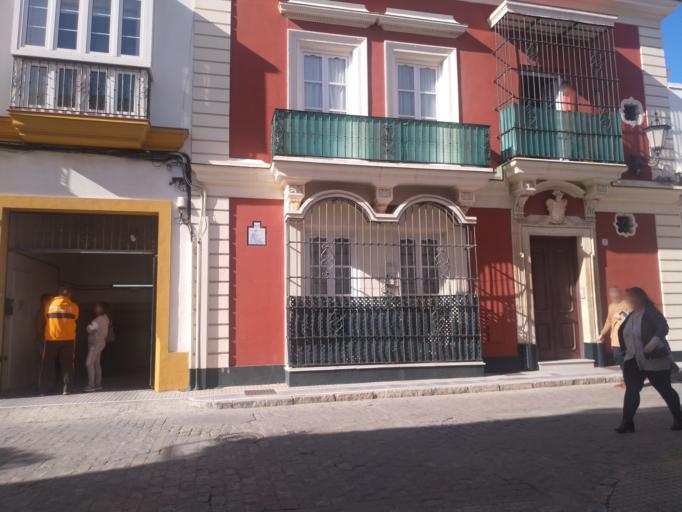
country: ES
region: Andalusia
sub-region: Provincia de Cadiz
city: San Fernando
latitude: 36.4685
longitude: -6.1941
